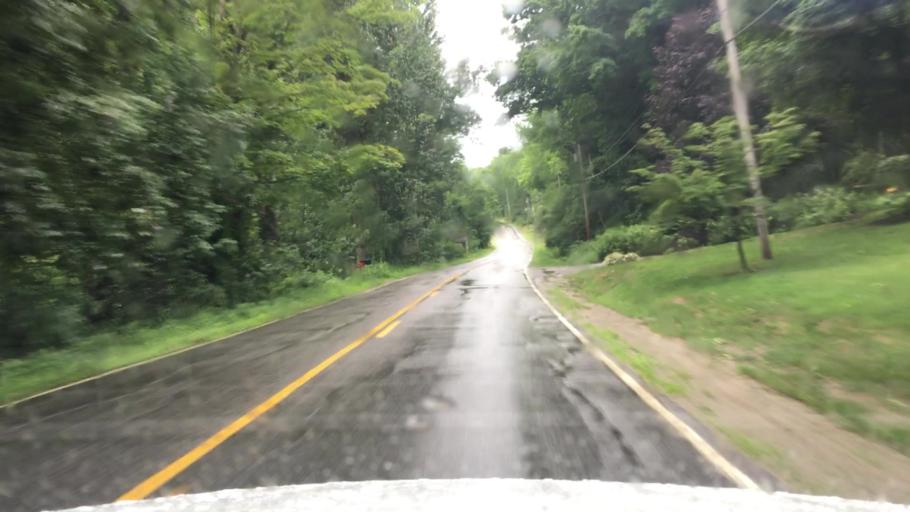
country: US
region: Maine
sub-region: Kennebec County
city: Winthrop
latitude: 44.3018
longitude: -69.9239
